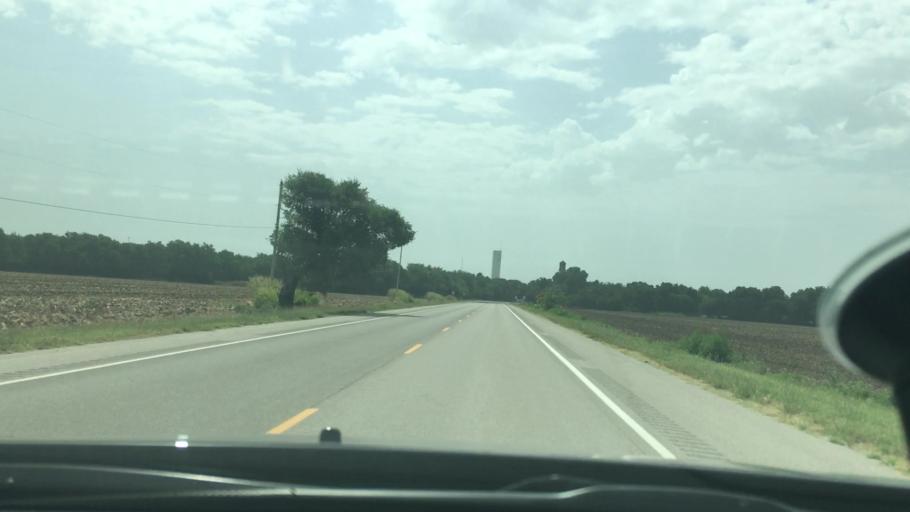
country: US
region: Oklahoma
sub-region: Garvin County
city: Pauls Valley
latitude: 34.8331
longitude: -97.2632
